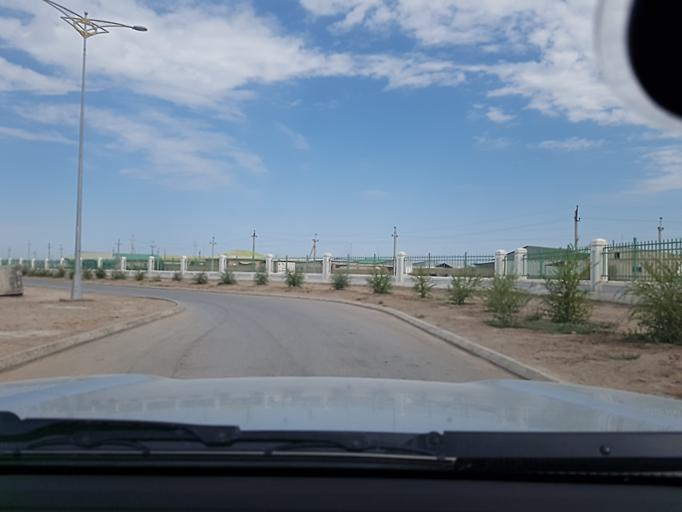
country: TM
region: Dasoguz
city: Dasoguz
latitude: 41.8801
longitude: 59.9529
